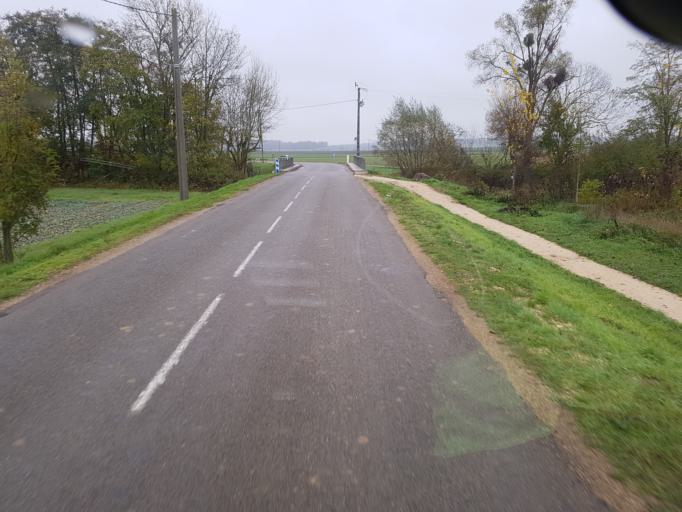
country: FR
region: Bourgogne
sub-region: Departement de la Cote-d'Or
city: Genlis
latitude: 47.2742
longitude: 5.2178
